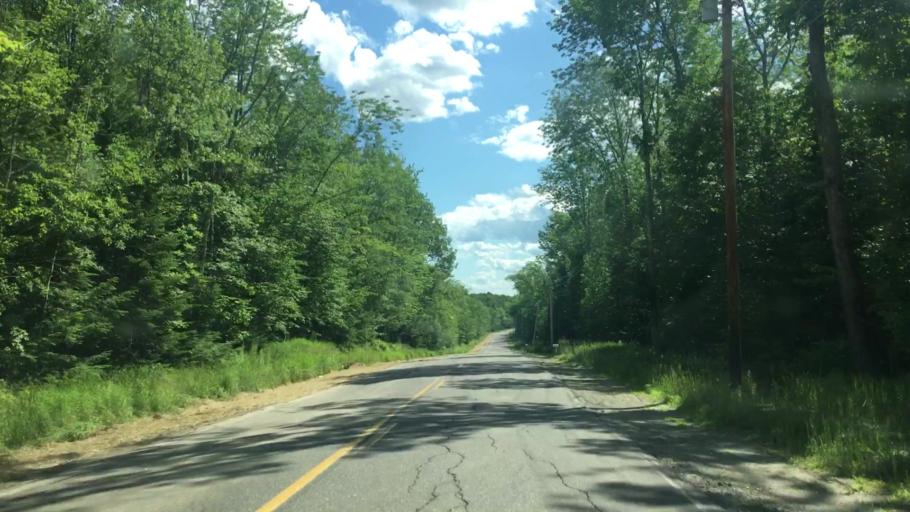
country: US
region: Maine
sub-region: Franklin County
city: Farmington
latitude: 44.6964
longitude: -70.1148
